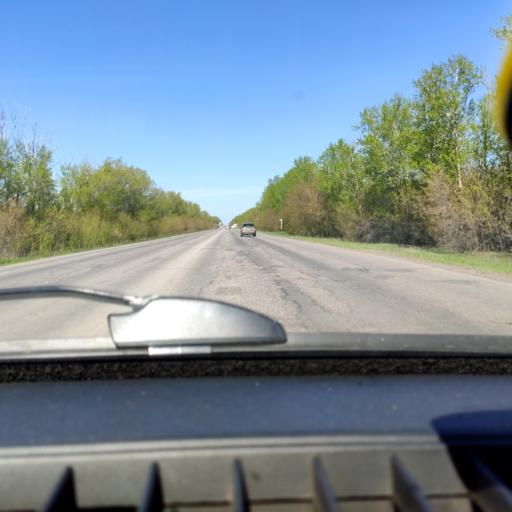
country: RU
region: Samara
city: Tol'yatti
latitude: 53.6123
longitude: 49.4122
